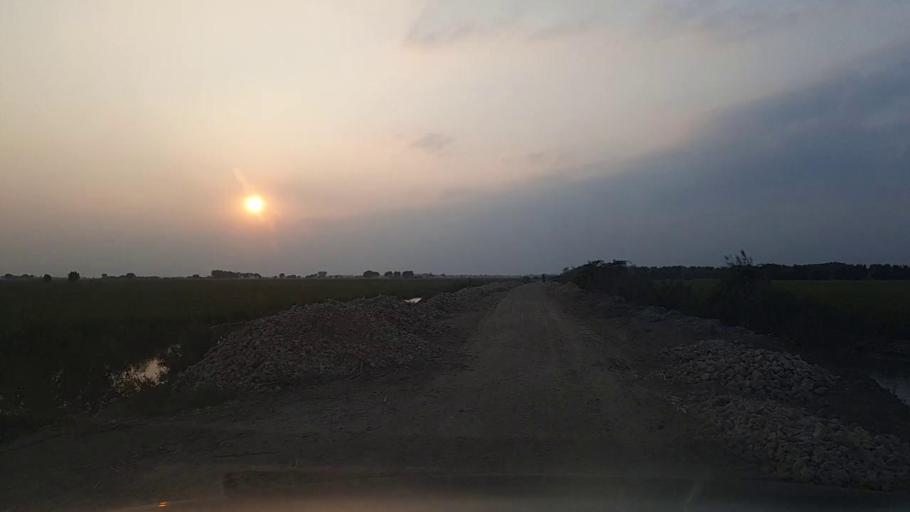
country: PK
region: Sindh
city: Jati
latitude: 24.5296
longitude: 68.4056
